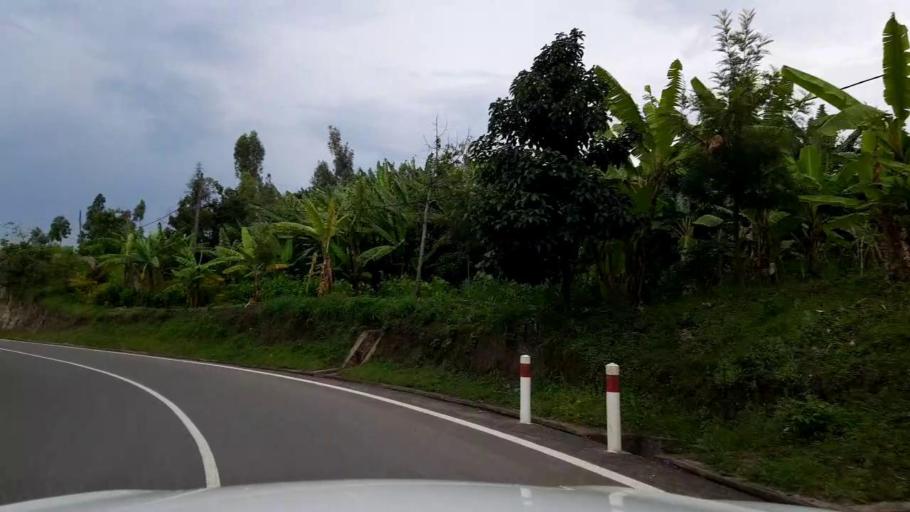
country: RW
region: Western Province
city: Kibuye
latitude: -2.0450
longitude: 29.4089
